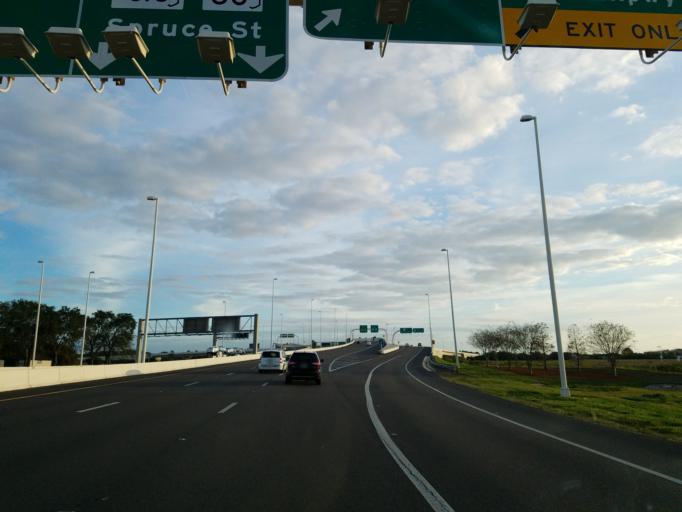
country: US
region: Florida
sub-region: Hillsborough County
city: Town 'n' Country
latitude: 27.9644
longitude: -82.5395
